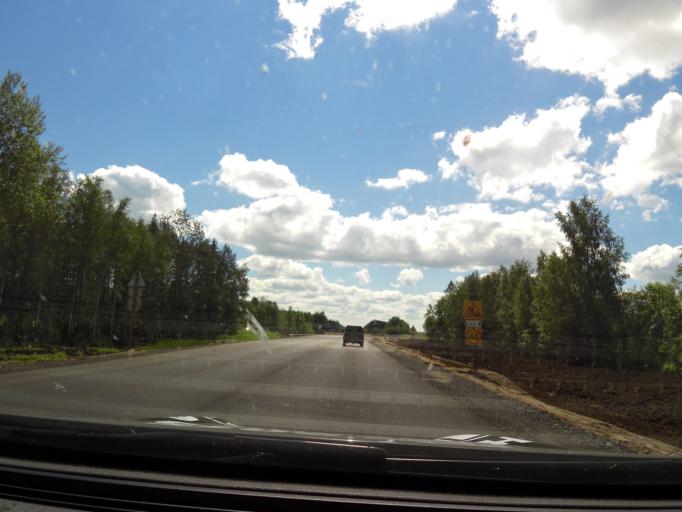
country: RU
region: Vologda
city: Molochnoye
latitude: 59.3276
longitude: 39.6823
